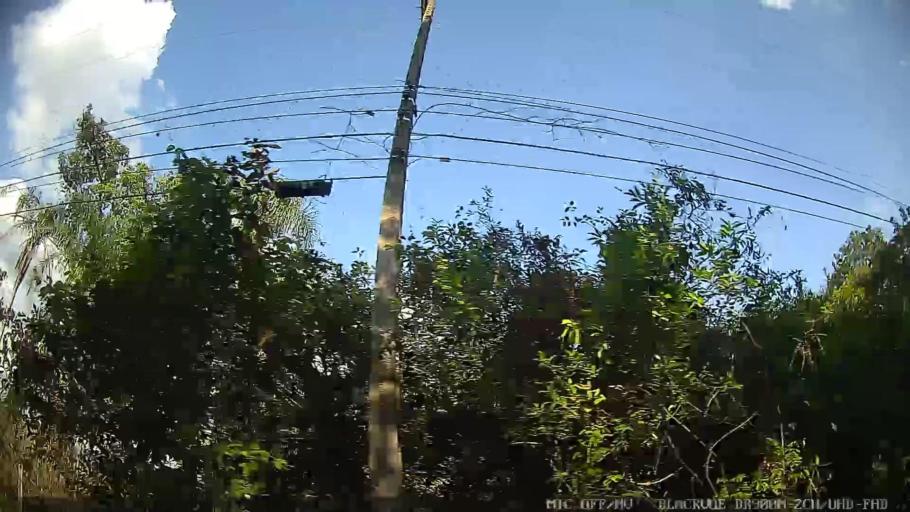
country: BR
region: Sao Paulo
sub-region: Braganca Paulista
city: Braganca Paulista
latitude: -22.9618
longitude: -46.5147
